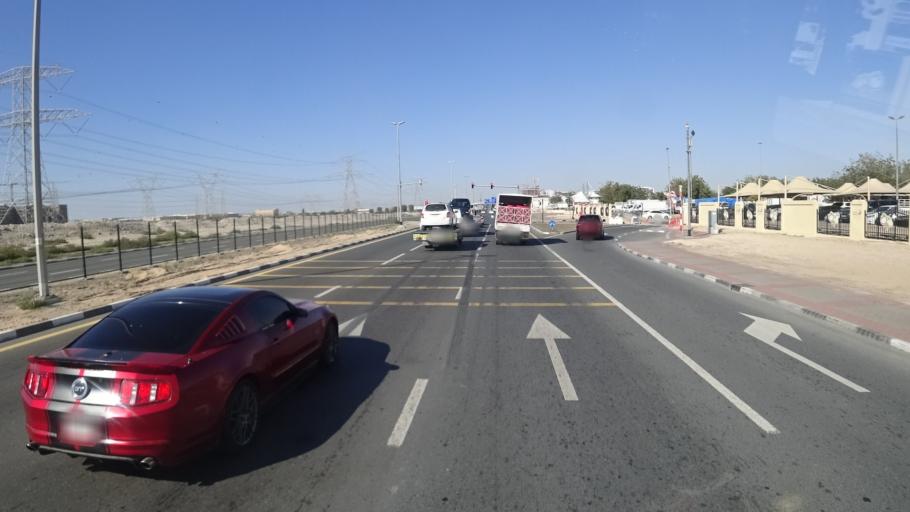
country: AE
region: Ash Shariqah
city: Sharjah
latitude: 25.1756
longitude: 55.3859
